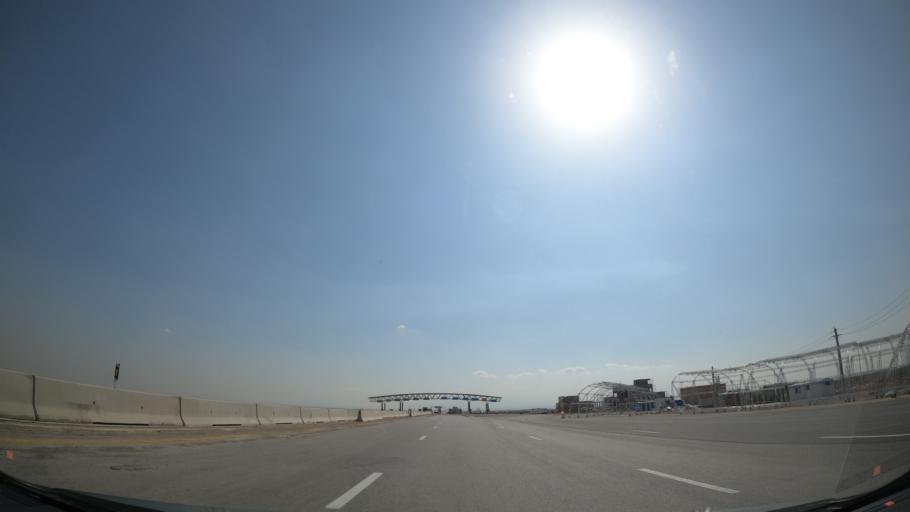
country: IR
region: Qazvin
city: Abyek
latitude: 35.9603
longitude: 50.4639
